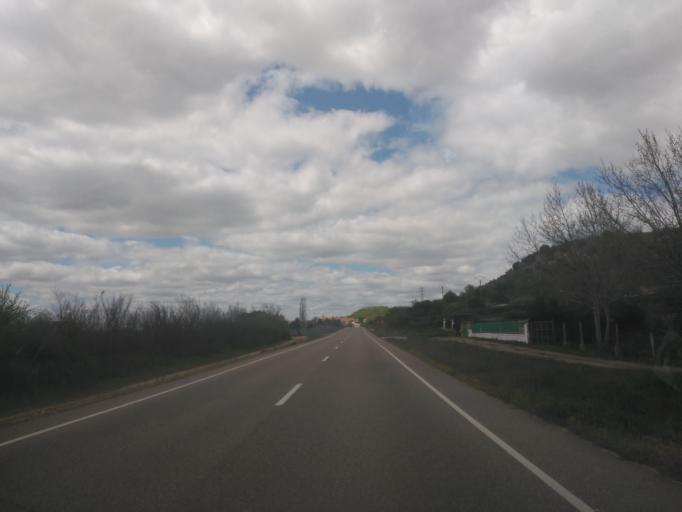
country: ES
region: Castille and Leon
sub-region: Provincia de Salamanca
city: Almenara de Tormes
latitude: 41.0594
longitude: -5.8088
